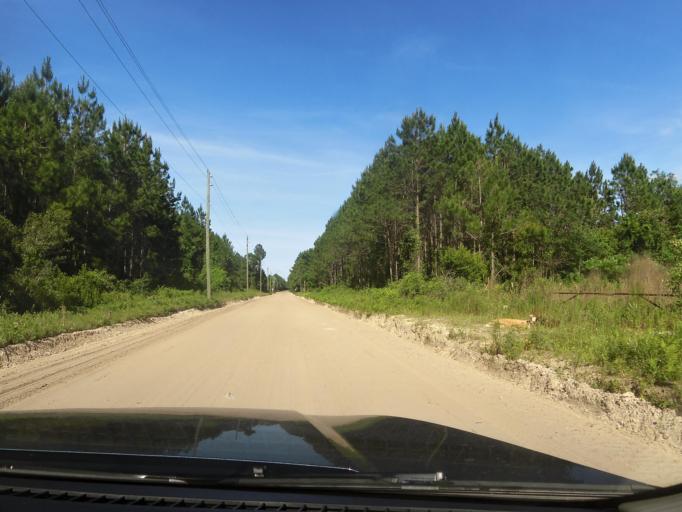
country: US
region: Florida
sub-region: Nassau County
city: Callahan
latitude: 30.5681
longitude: -81.7783
